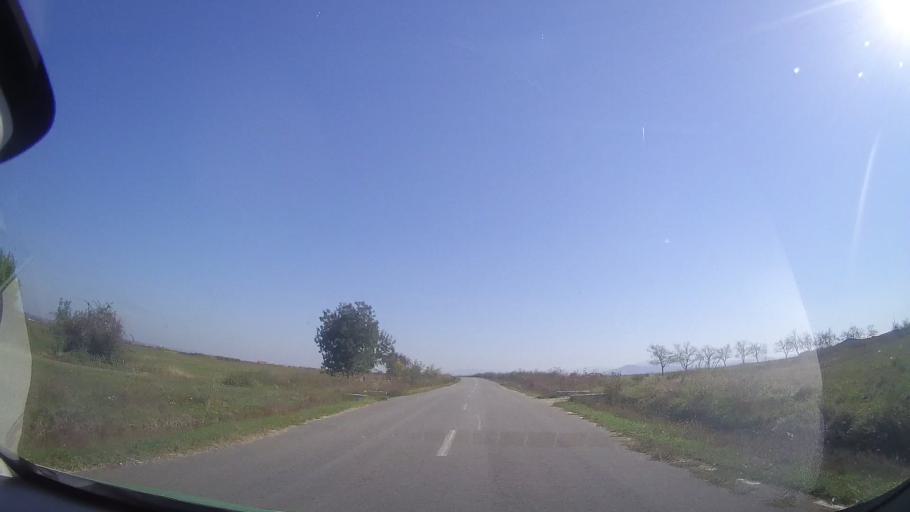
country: RO
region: Timis
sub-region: Comuna Bethausen
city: Bethausen
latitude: 45.7941
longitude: 21.9727
